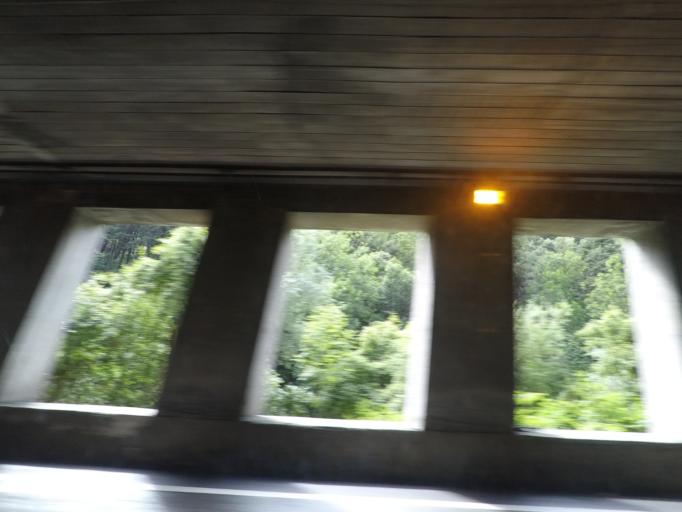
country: IT
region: Aosta Valley
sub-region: Valle d'Aosta
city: Antey-Saint-Andre
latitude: 45.7859
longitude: 7.5919
